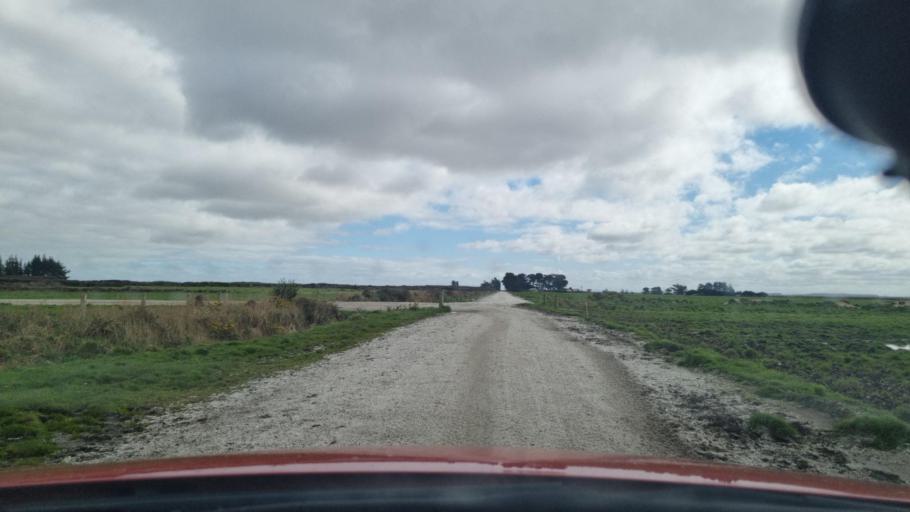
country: NZ
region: Southland
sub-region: Invercargill City
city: Bluff
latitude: -46.5615
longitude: 168.4924
